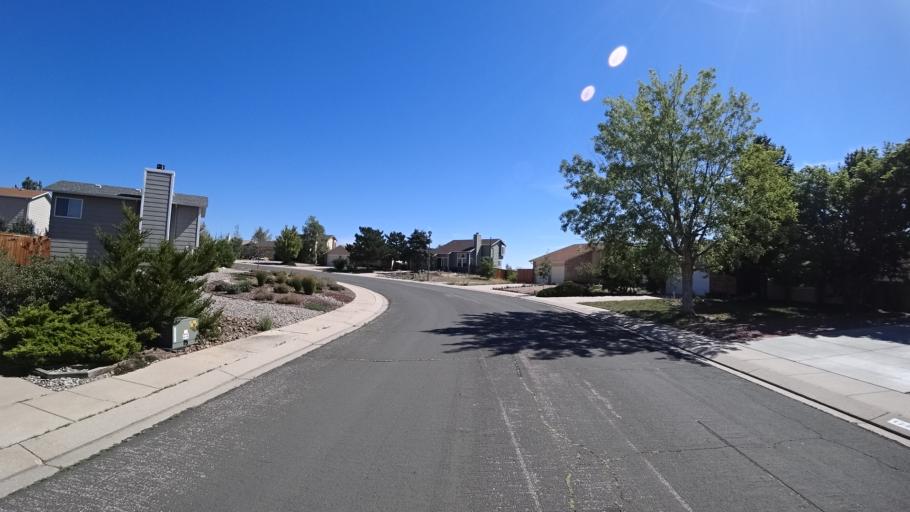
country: US
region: Colorado
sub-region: El Paso County
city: Black Forest
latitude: 38.9459
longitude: -104.7482
